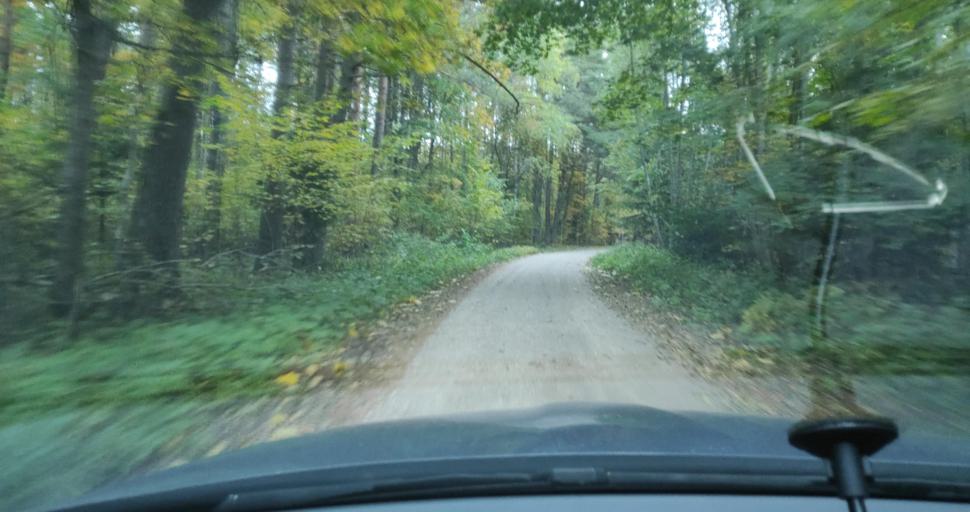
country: LV
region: Kandava
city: Kandava
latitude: 57.0217
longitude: 22.7592
